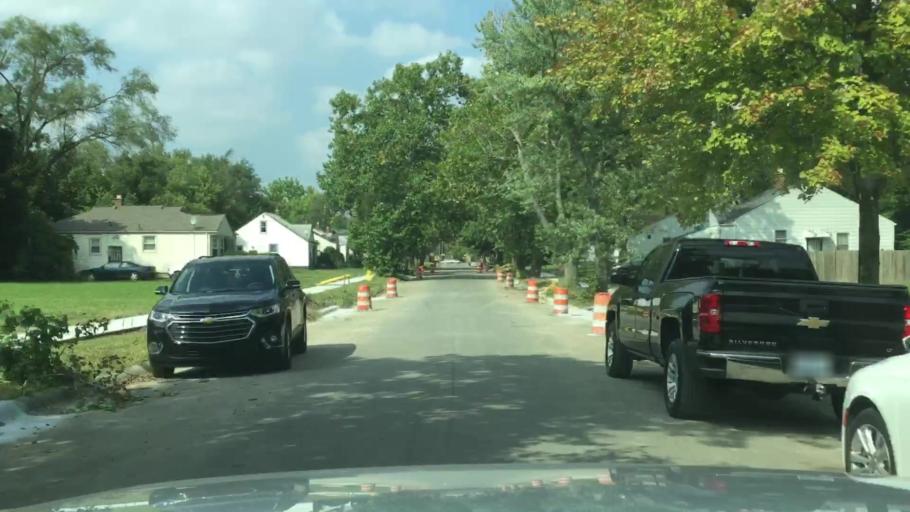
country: US
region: Michigan
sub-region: Wayne County
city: Dearborn
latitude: 42.3619
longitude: -83.2003
